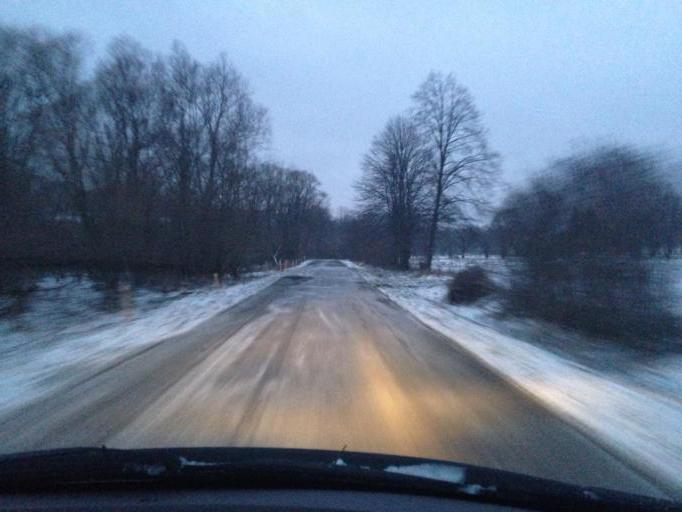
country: PL
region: Subcarpathian Voivodeship
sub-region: Powiat jasielski
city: Krempna
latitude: 49.5294
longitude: 21.5540
